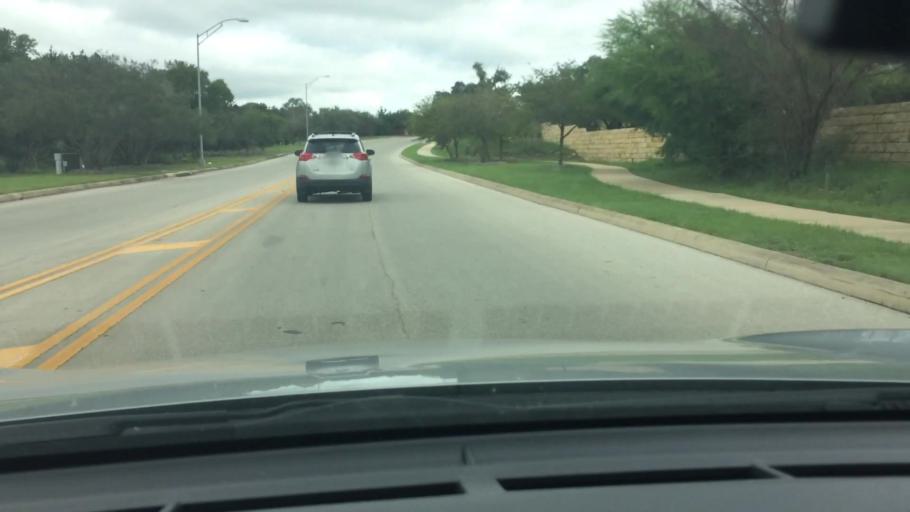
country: US
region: Texas
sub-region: Bexar County
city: Timberwood Park
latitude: 29.6583
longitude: -98.4008
